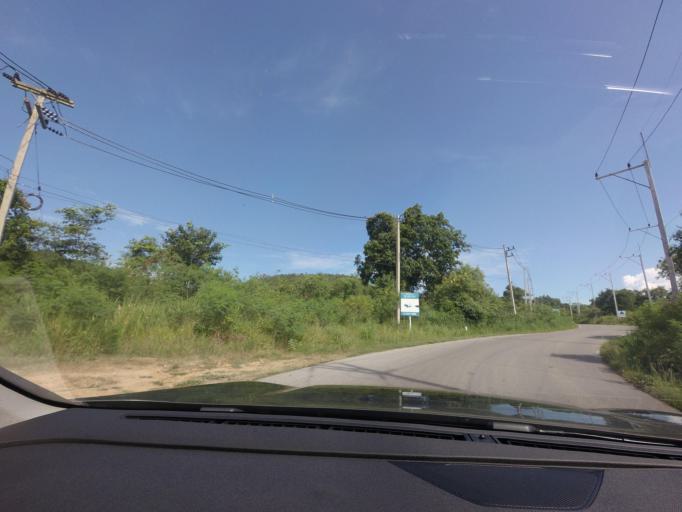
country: TH
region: Prachuap Khiri Khan
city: Hua Hin
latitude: 12.4955
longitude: 99.9415
